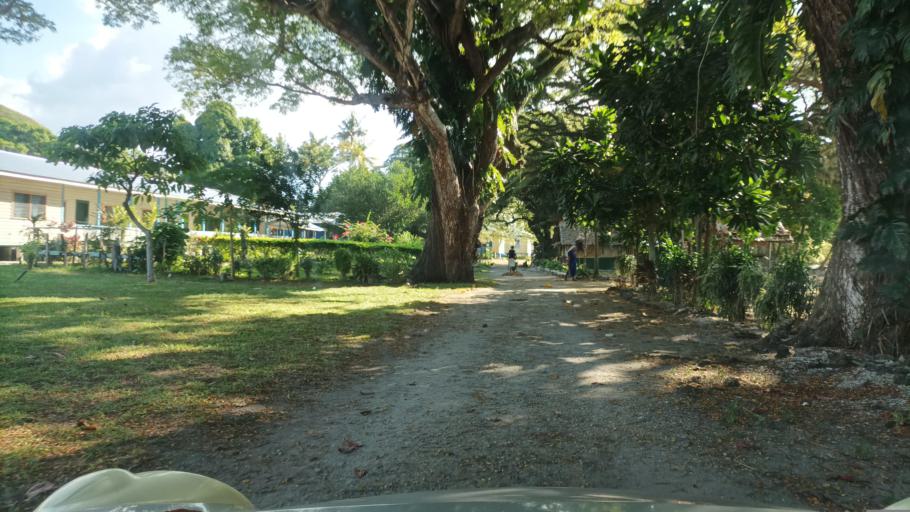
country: SB
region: Guadalcanal
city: Honiara
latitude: -9.2527
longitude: 159.6965
